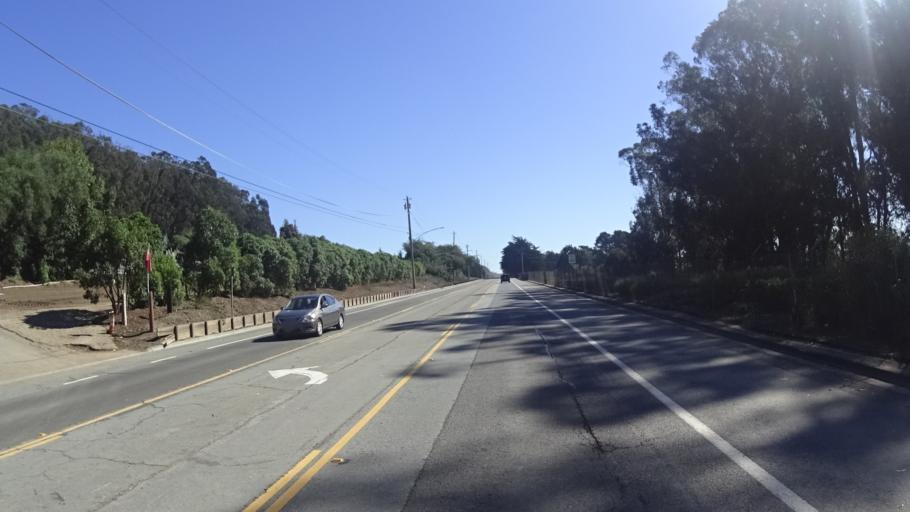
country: US
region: California
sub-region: San Mateo County
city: Colma
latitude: 37.6766
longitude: -122.4452
